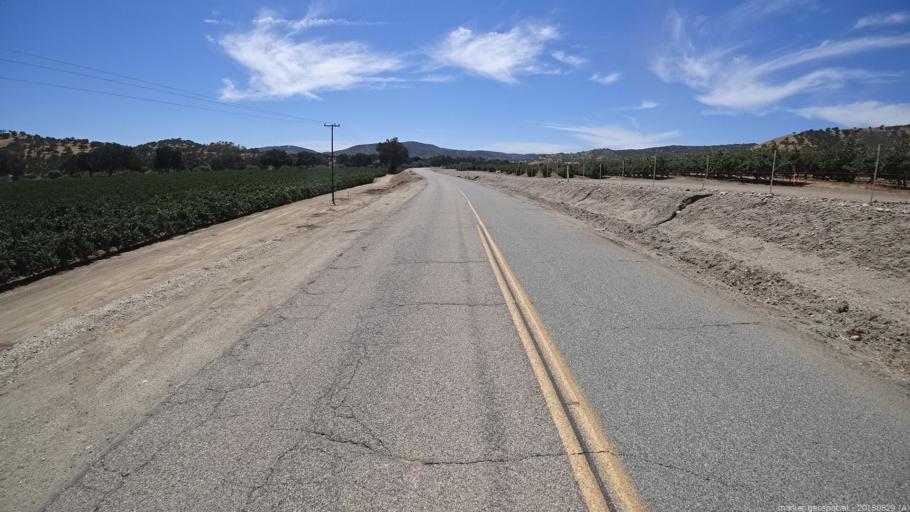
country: US
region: California
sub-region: San Luis Obispo County
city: Lake Nacimiento
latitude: 35.8121
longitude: -120.8475
